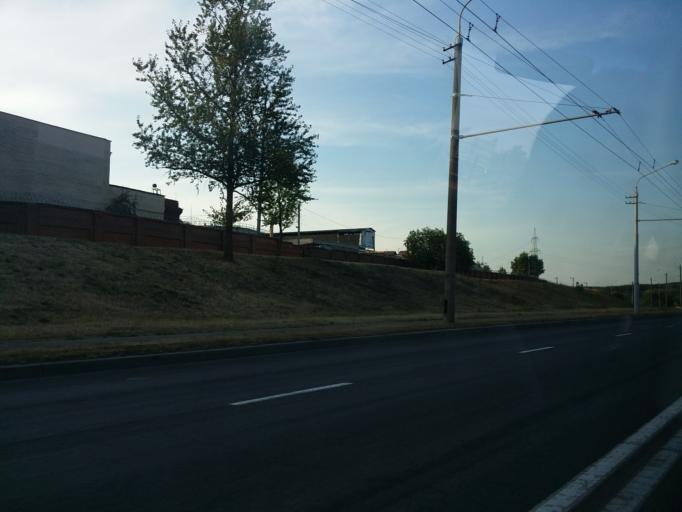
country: BY
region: Minsk
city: Vyaliki Trastsyanets
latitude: 53.8783
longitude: 27.6545
